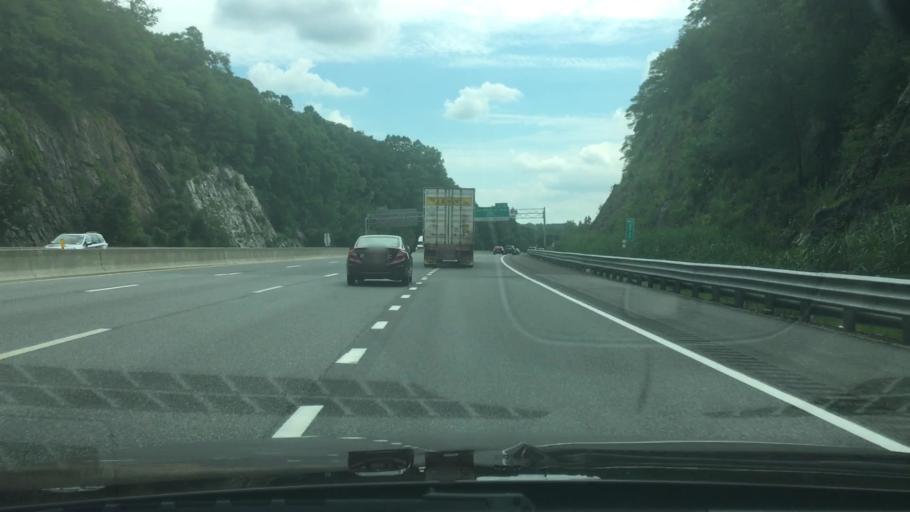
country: US
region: New York
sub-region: Westchester County
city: Elmsford
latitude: 41.0523
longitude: -73.8335
